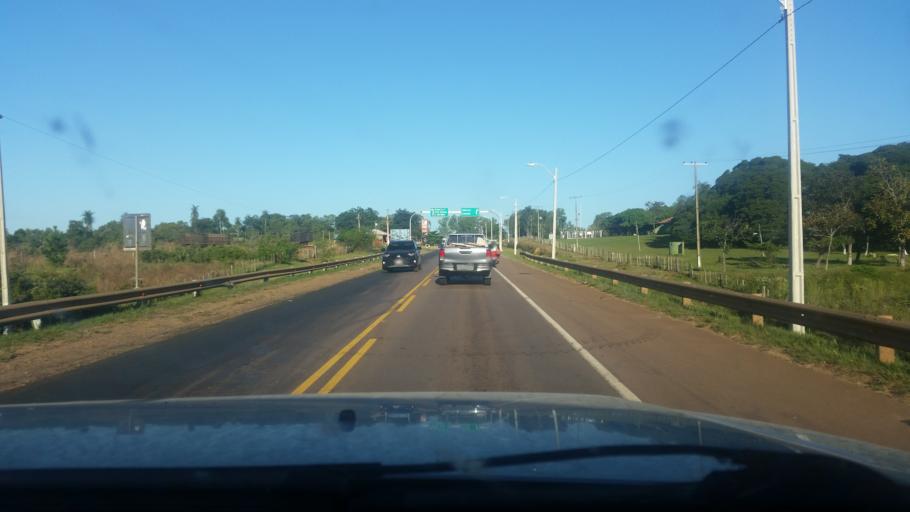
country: PY
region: Guaira
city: Villarrica
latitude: -25.7529
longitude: -56.4396
